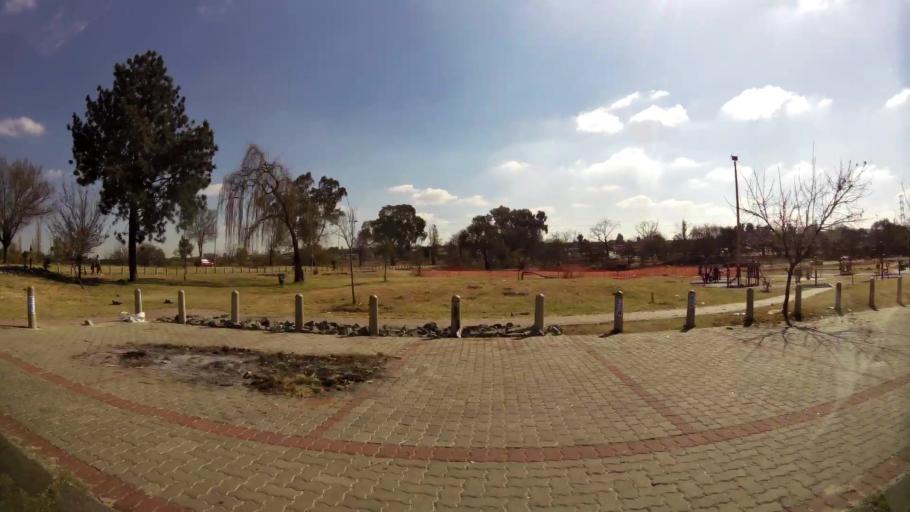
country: ZA
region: Gauteng
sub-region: City of Johannesburg Metropolitan Municipality
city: Soweto
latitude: -26.2411
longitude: 27.8805
